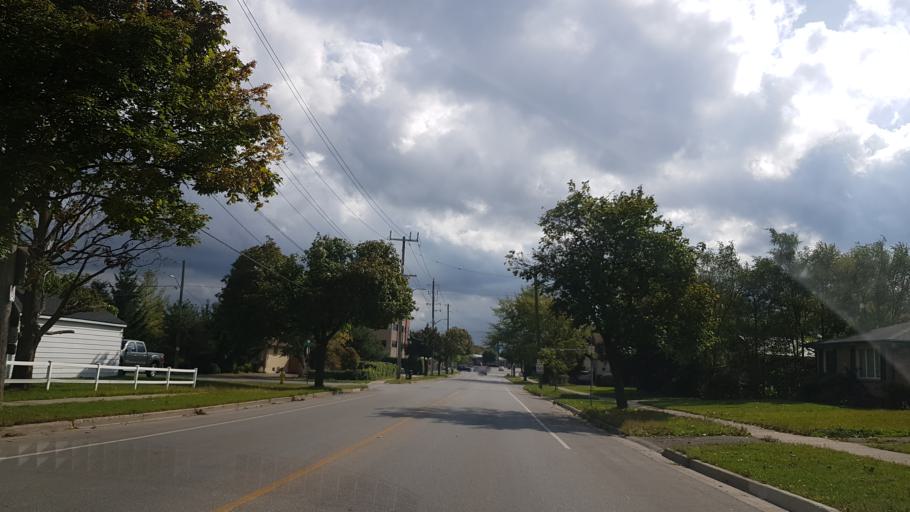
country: CA
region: Ontario
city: London
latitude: 42.9444
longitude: -81.2374
